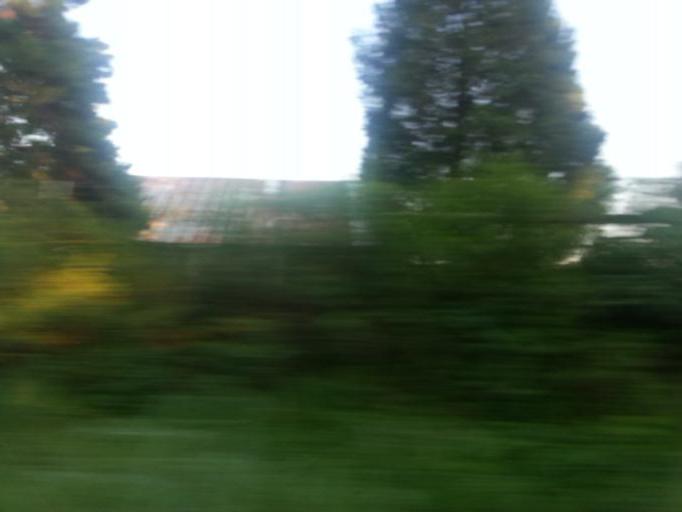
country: US
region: Tennessee
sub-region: Roane County
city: Rockwood
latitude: 35.7504
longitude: -84.6105
